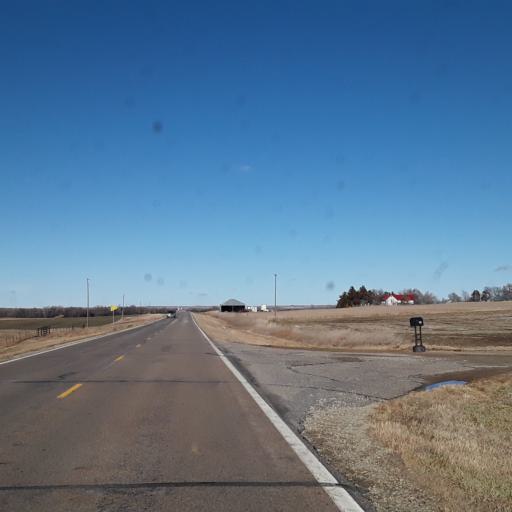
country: US
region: Kansas
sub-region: Lincoln County
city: Lincoln
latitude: 38.9631
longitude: -98.1512
